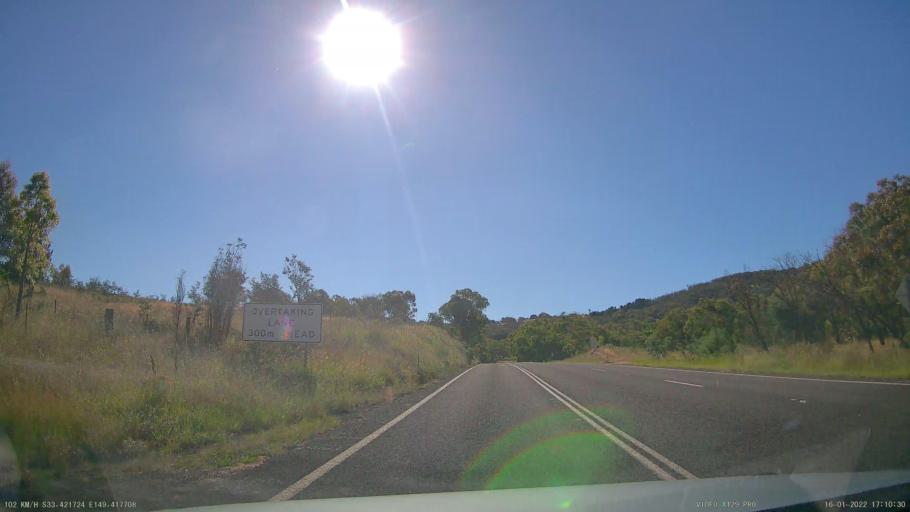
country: AU
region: New South Wales
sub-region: Bathurst Regional
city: Eglinton
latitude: -33.4217
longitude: 149.4174
